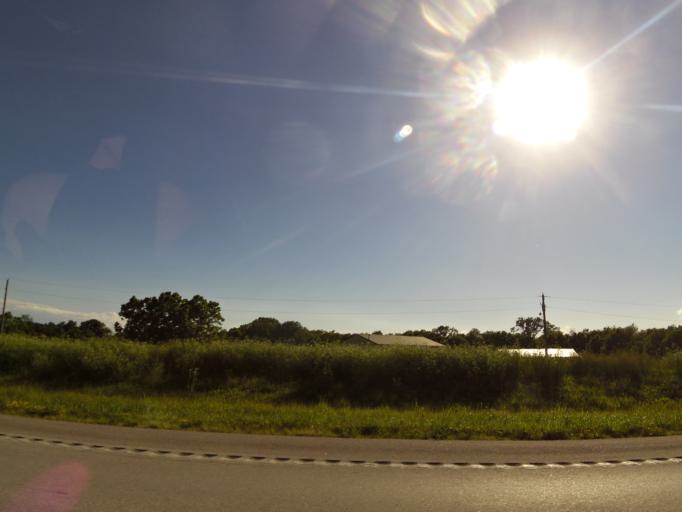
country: US
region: Missouri
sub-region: Pike County
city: Bowling Green
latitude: 39.4198
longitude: -91.2523
